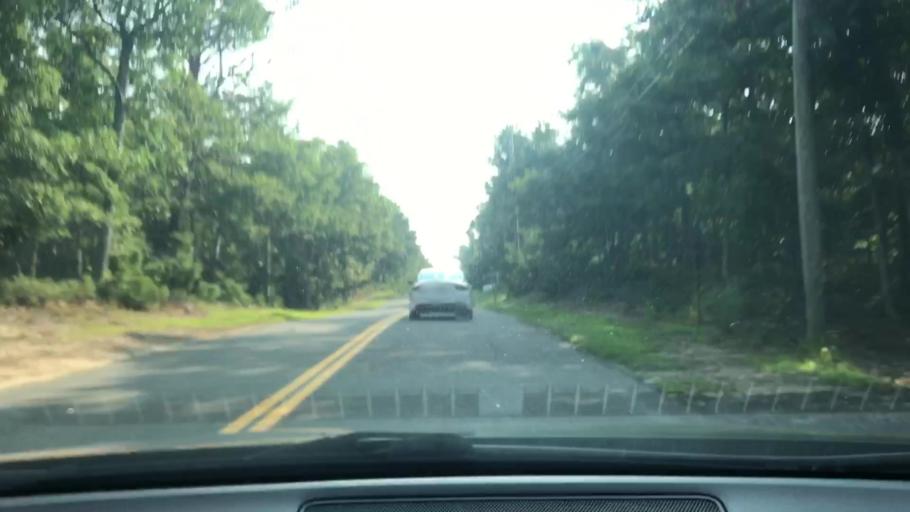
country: US
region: New York
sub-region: Suffolk County
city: North Sea
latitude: 40.9577
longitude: -72.3770
